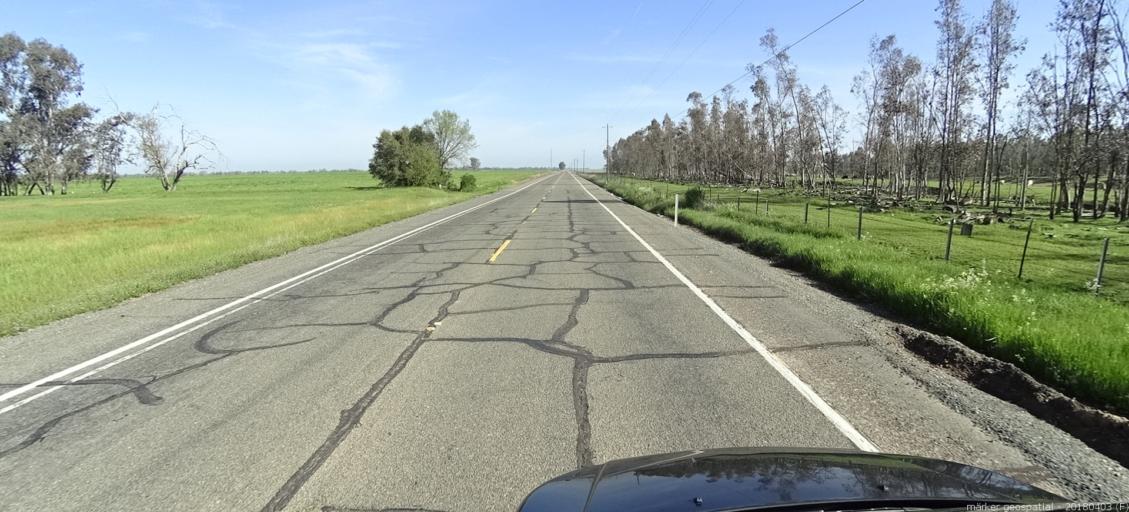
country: US
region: California
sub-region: Sacramento County
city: Clay
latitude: 38.3544
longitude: -121.1684
